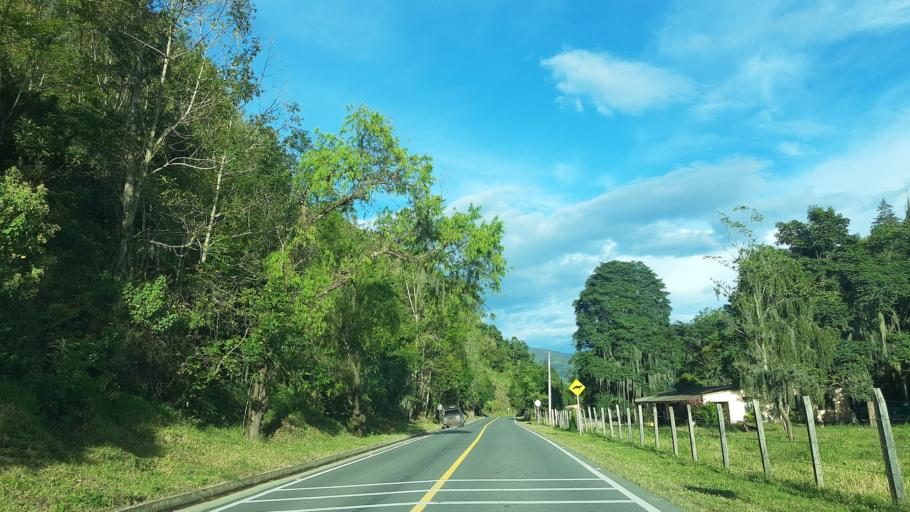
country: CO
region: Cundinamarca
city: Macheta
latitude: 5.0759
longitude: -73.5754
